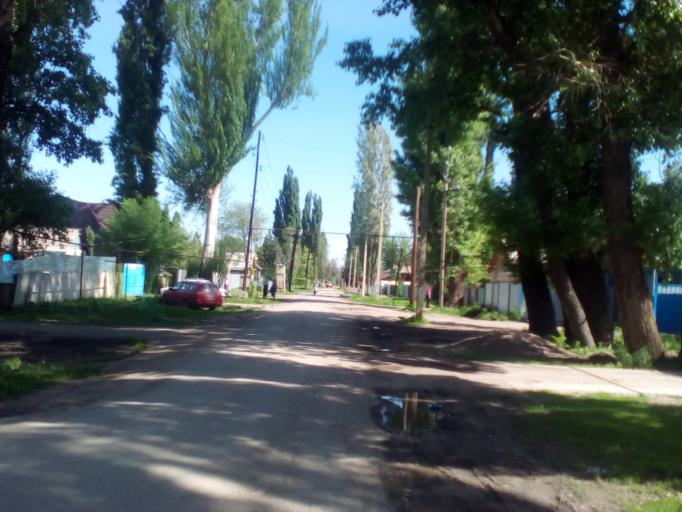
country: KZ
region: Almaty Oblysy
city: Burunday
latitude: 43.2234
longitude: 76.3163
